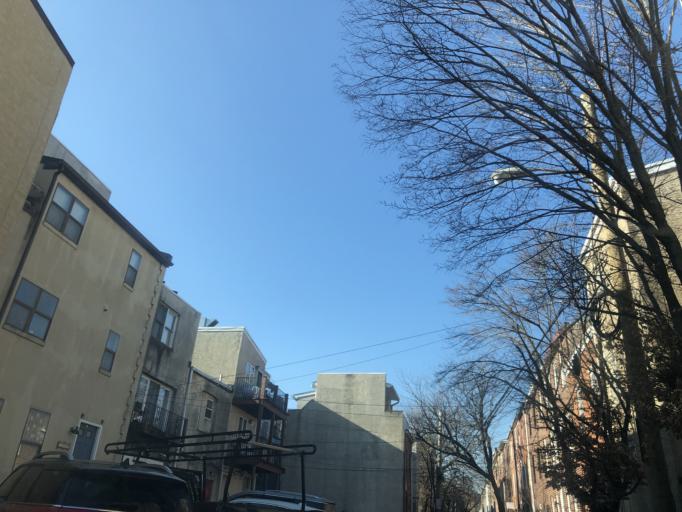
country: US
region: Pennsylvania
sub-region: Philadelphia County
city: Philadelphia
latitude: 39.9442
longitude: -75.1672
